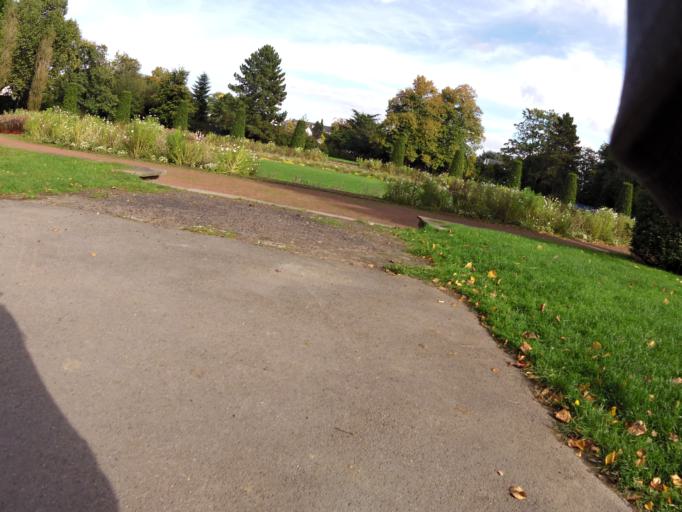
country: DE
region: North Rhine-Westphalia
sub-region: Regierungsbezirk Dusseldorf
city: Dusseldorf
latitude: 51.2587
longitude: 6.7492
